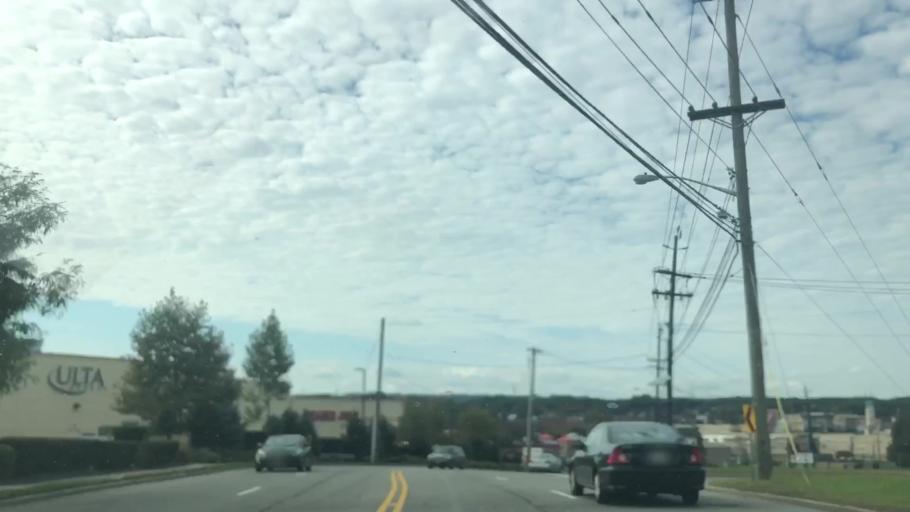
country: US
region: New Jersey
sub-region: Essex County
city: Nutley
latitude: 40.8368
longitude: -74.1500
